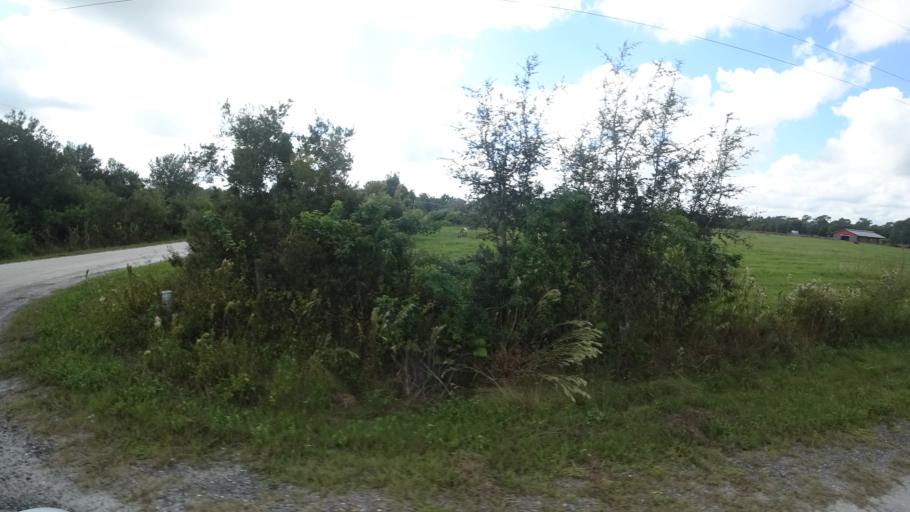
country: US
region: Florida
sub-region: Sarasota County
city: Lake Sarasota
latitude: 27.4013
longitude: -82.2665
